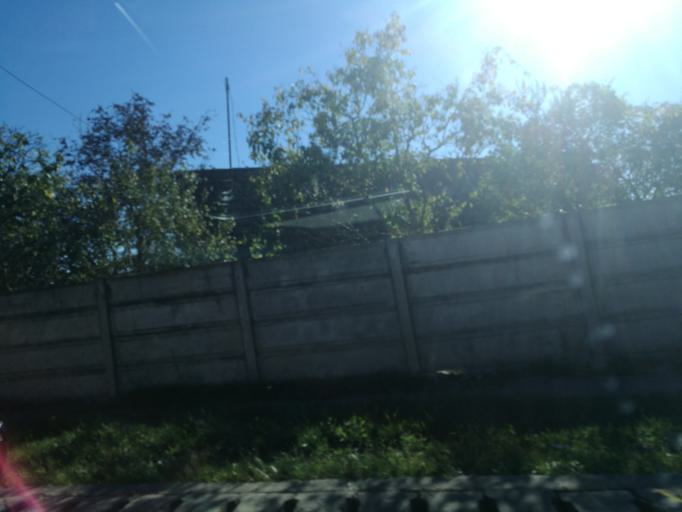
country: RO
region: Brasov
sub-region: Comuna Mandra
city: Mandra
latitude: 45.8233
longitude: 25.0432
